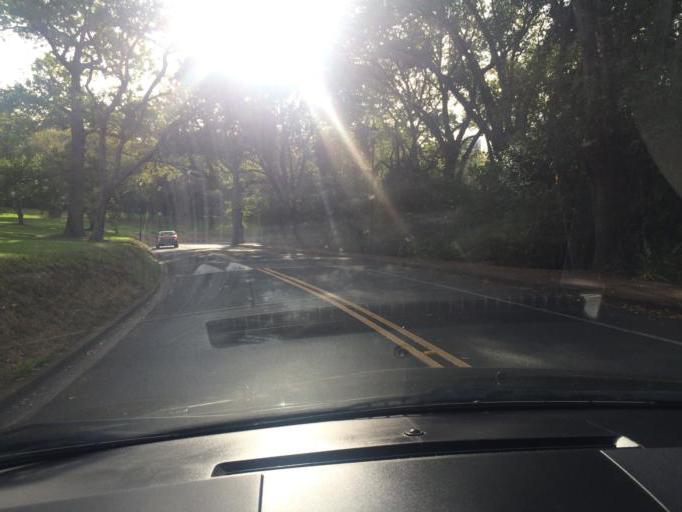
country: NZ
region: Auckland
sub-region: Auckland
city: Auckland
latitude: -36.8567
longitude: 174.7767
